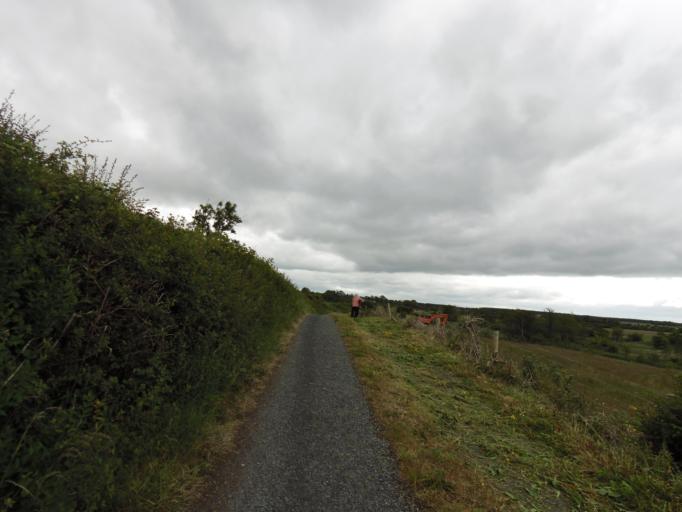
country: IE
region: Connaught
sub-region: County Galway
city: Athenry
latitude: 53.3151
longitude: -8.7292
